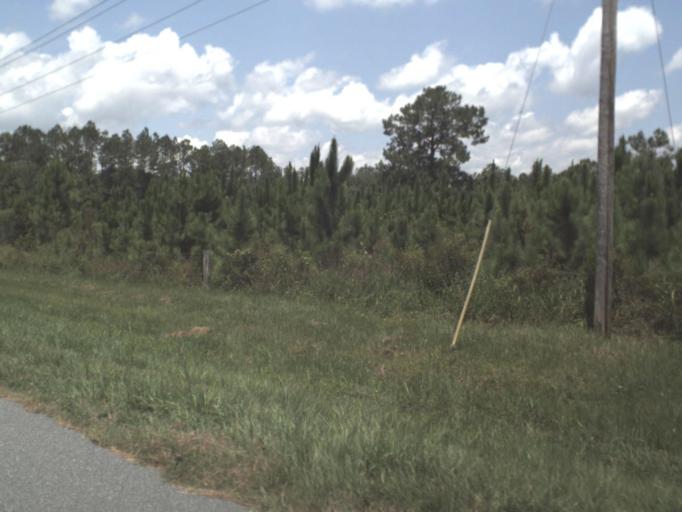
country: US
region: Florida
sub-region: Union County
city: Lake Butler
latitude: 30.0099
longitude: -82.4523
